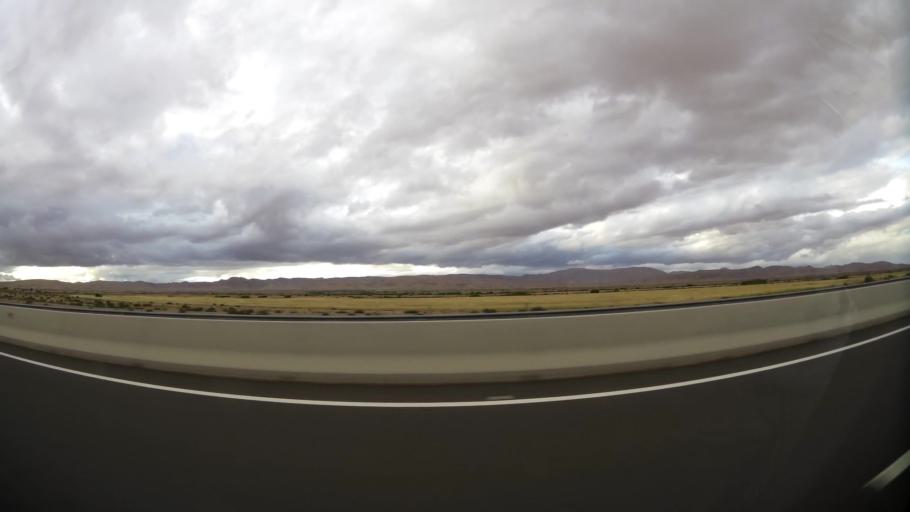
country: MA
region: Taza-Al Hoceima-Taounate
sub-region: Taza
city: Guercif
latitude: 34.3050
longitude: -3.6246
